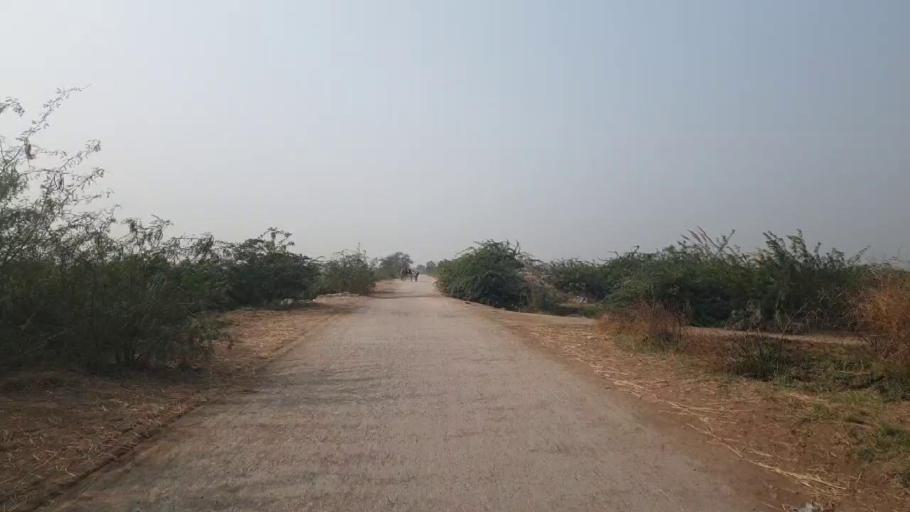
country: PK
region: Sindh
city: Tando Jam
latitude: 25.2911
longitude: 68.4999
